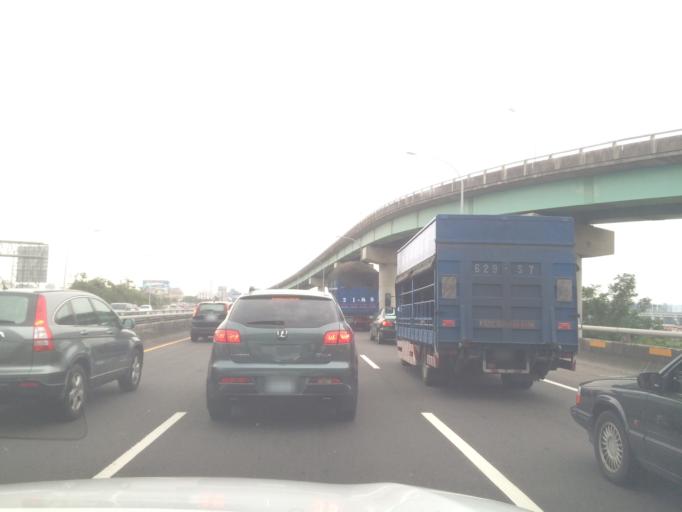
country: TW
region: Taiwan
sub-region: Taichung City
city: Taichung
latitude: 24.1201
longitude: 120.6196
